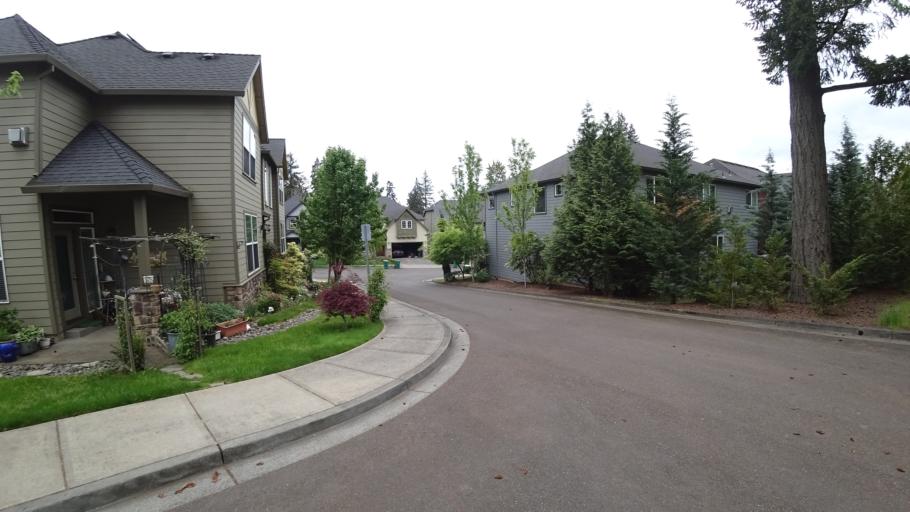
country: US
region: Oregon
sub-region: Washington County
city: Beaverton
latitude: 45.4496
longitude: -122.8356
